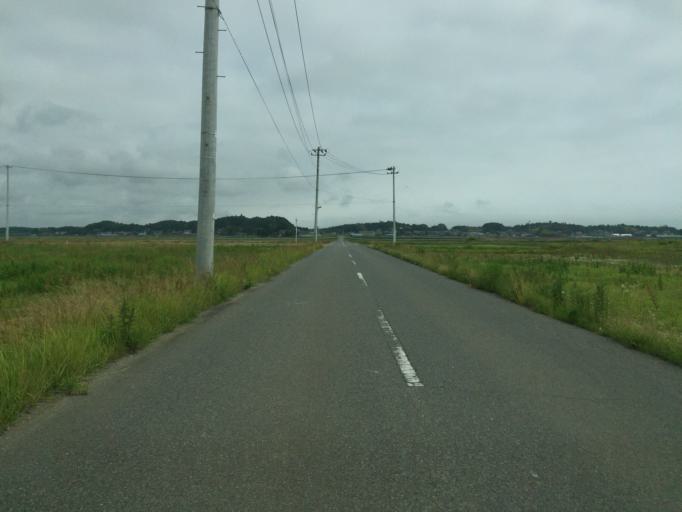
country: JP
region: Fukushima
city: Namie
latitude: 37.6961
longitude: 140.9964
